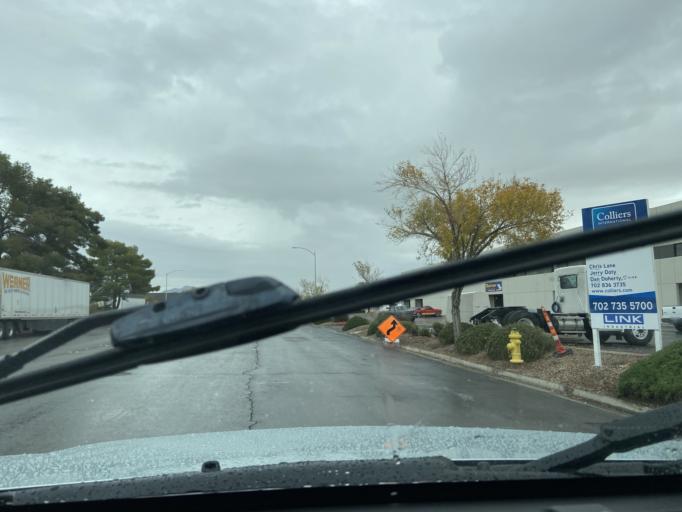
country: US
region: Nevada
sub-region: Clark County
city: Nellis Air Force Base
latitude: 36.2425
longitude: -115.0958
